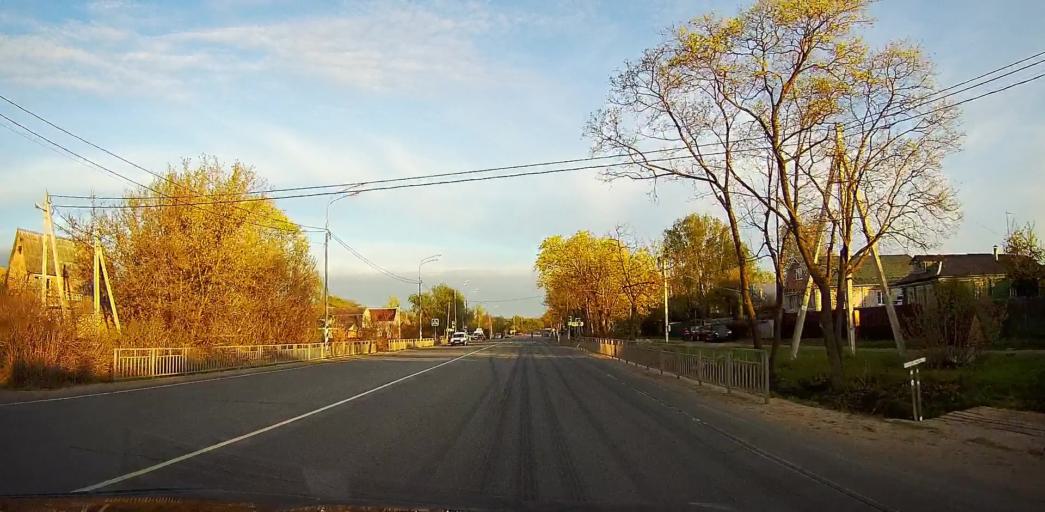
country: RU
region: Moskovskaya
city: Voskresensk
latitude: 55.2076
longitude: 38.6083
